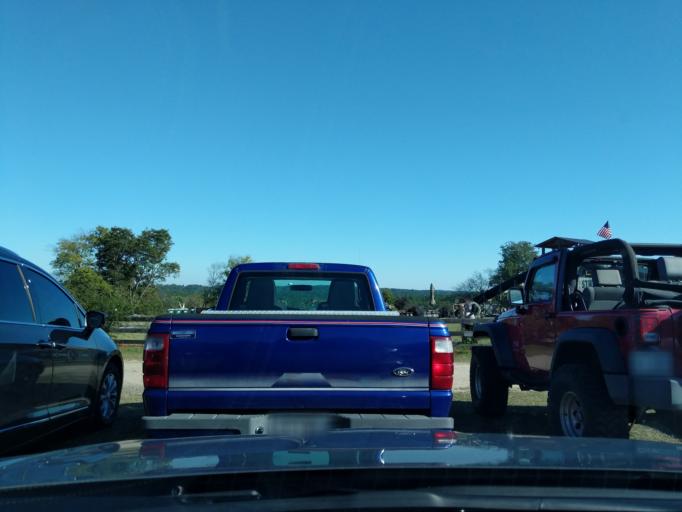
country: US
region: Georgia
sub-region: Columbia County
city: Grovetown
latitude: 33.4688
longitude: -82.1550
